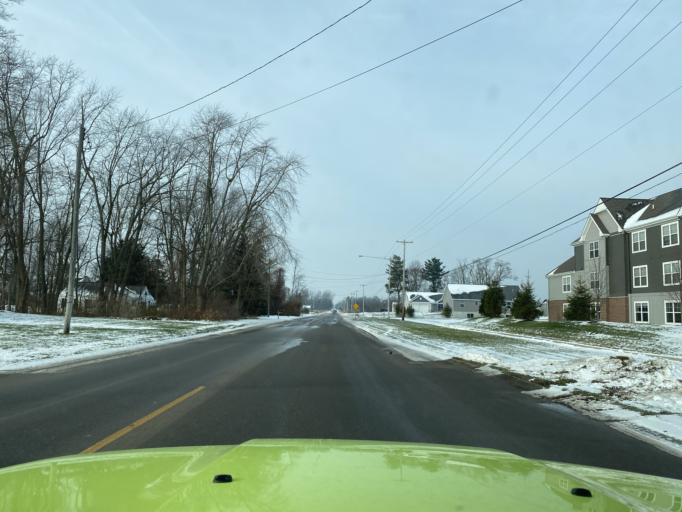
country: US
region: Michigan
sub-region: Ottawa County
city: Allendale
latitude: 42.9578
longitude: -85.9164
